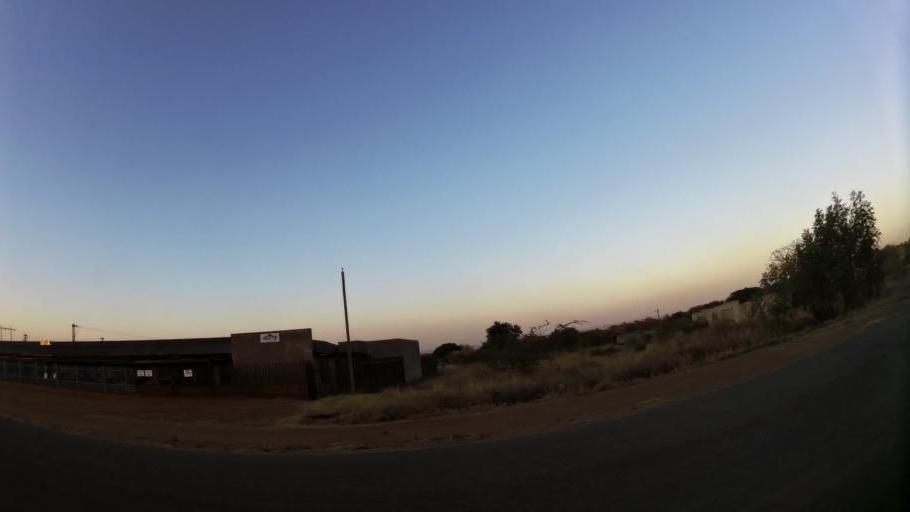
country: ZA
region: North-West
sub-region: Bojanala Platinum District Municipality
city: Rustenburg
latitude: -25.6178
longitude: 27.1948
